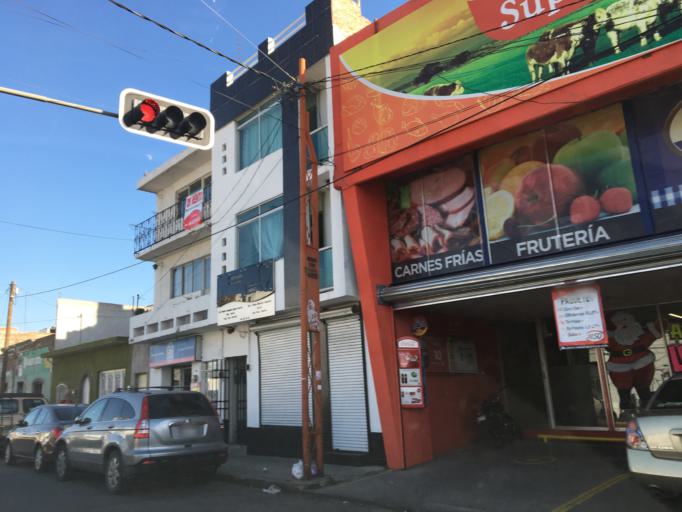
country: MX
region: San Luis Potosi
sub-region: San Luis Potosi
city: San Luis Potosi
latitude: 22.1444
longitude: -100.9922
